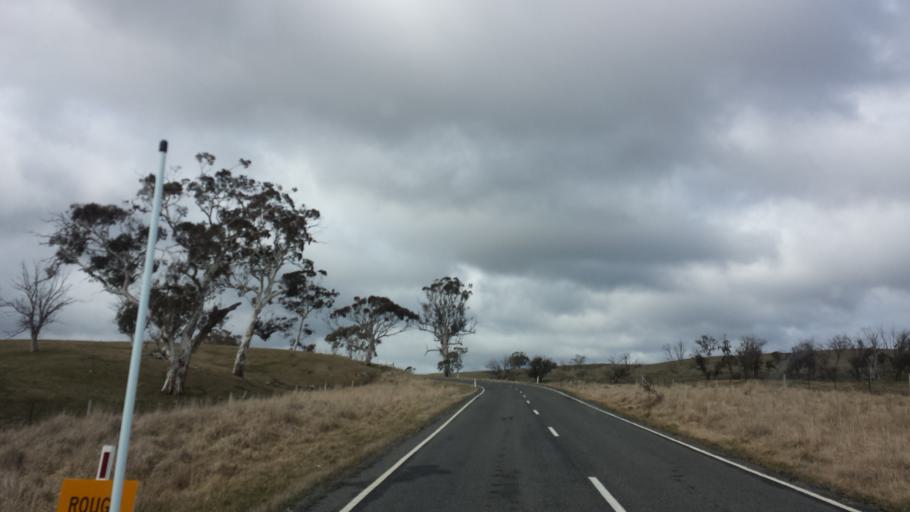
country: AU
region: Victoria
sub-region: Alpine
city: Mount Beauty
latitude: -37.1209
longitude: 147.4417
